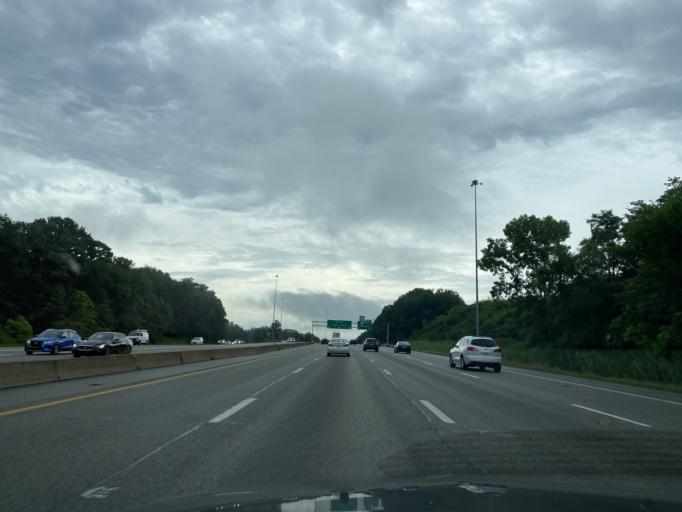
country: US
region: Ohio
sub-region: Summit County
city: Montrose-Ghent
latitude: 41.1305
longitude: -81.6456
